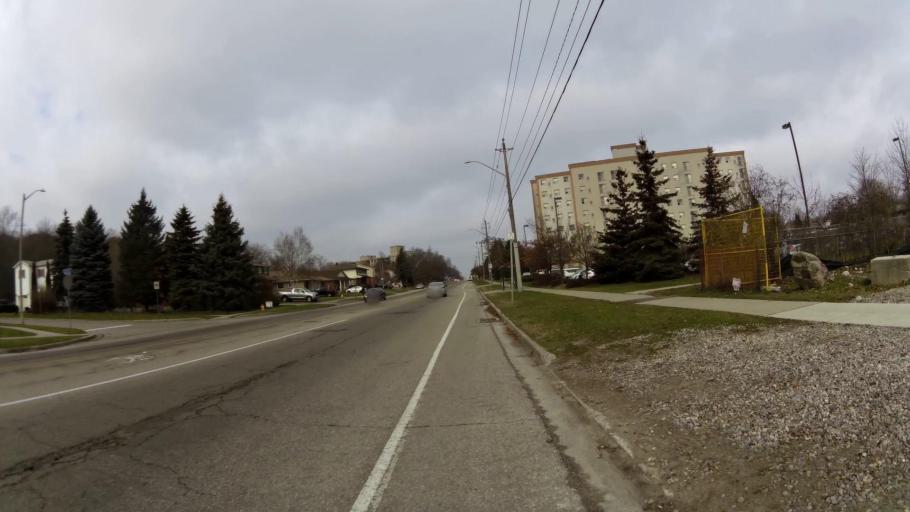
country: CA
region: Ontario
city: Kitchener
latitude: 43.4169
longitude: -80.4809
